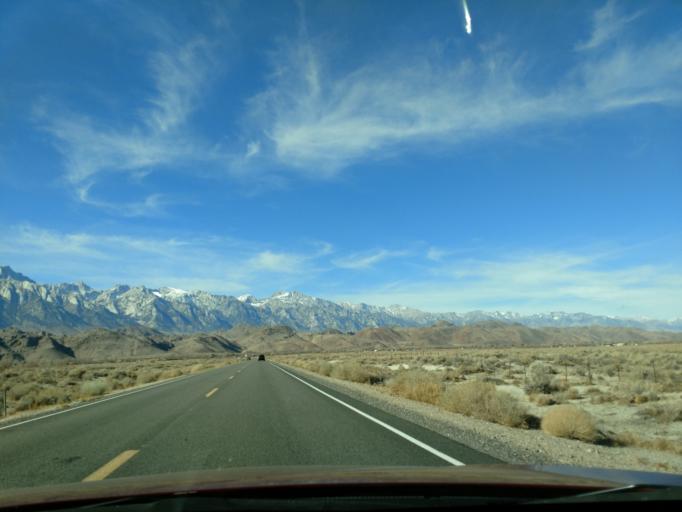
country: US
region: California
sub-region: Inyo County
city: Lone Pine
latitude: 36.5783
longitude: -118.0335
